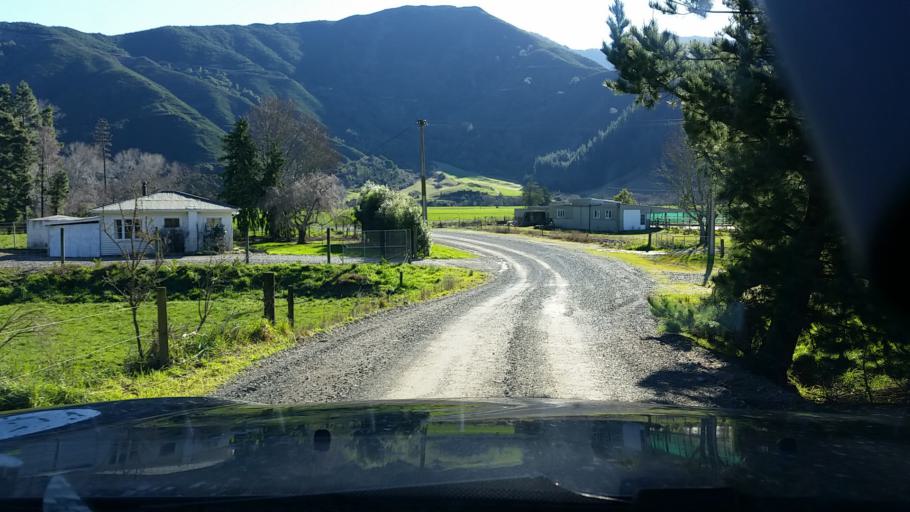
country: NZ
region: Marlborough
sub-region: Marlborough District
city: Picton
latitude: -41.2744
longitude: 173.7310
